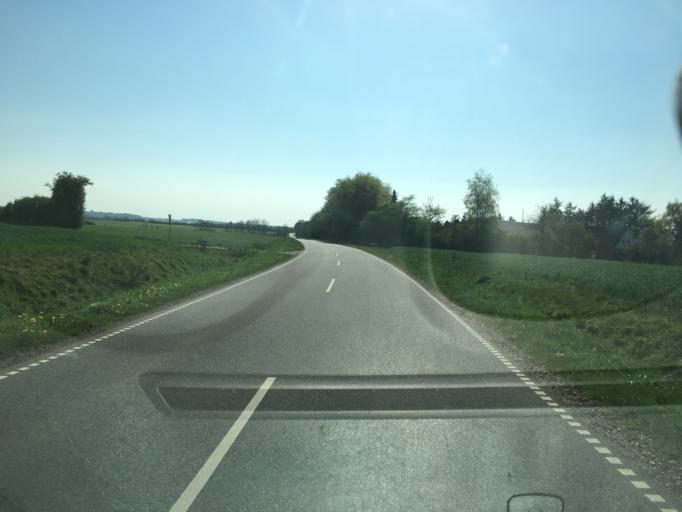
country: DK
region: South Denmark
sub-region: Haderslev Kommune
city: Vojens
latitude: 55.3003
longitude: 9.2551
